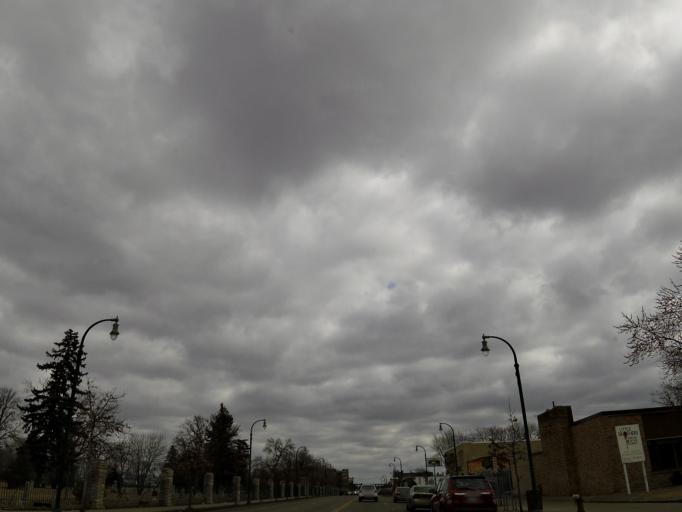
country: US
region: Minnesota
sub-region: Hennepin County
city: Minneapolis
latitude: 44.9484
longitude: -93.2463
